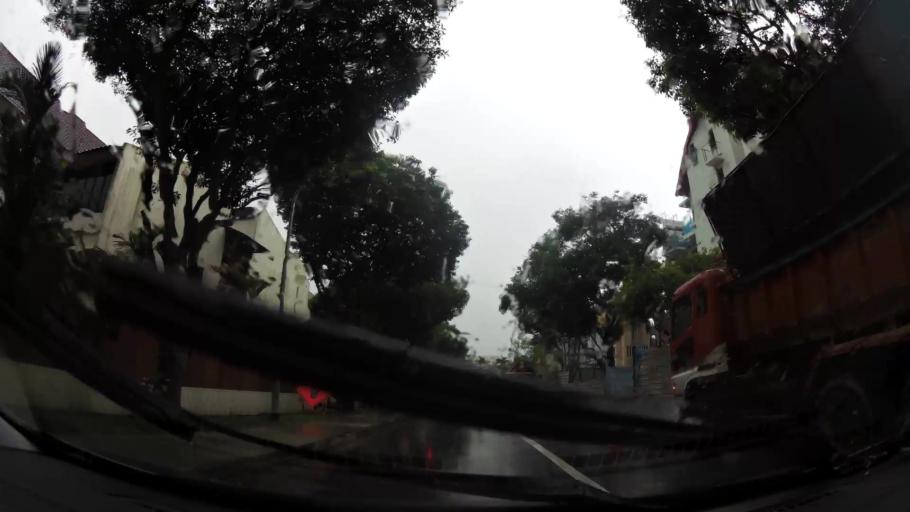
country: MY
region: Johor
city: Kampung Pasir Gudang Baru
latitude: 1.3921
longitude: 103.8515
